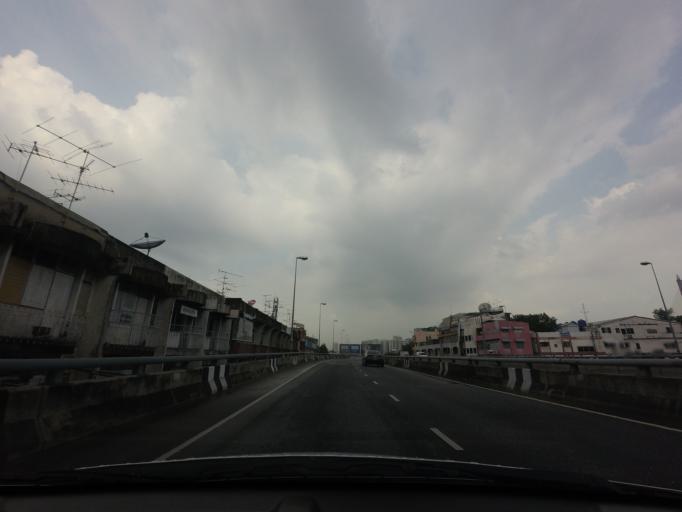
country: TH
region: Bangkok
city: Phra Nakhon
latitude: 13.7706
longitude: 100.4877
